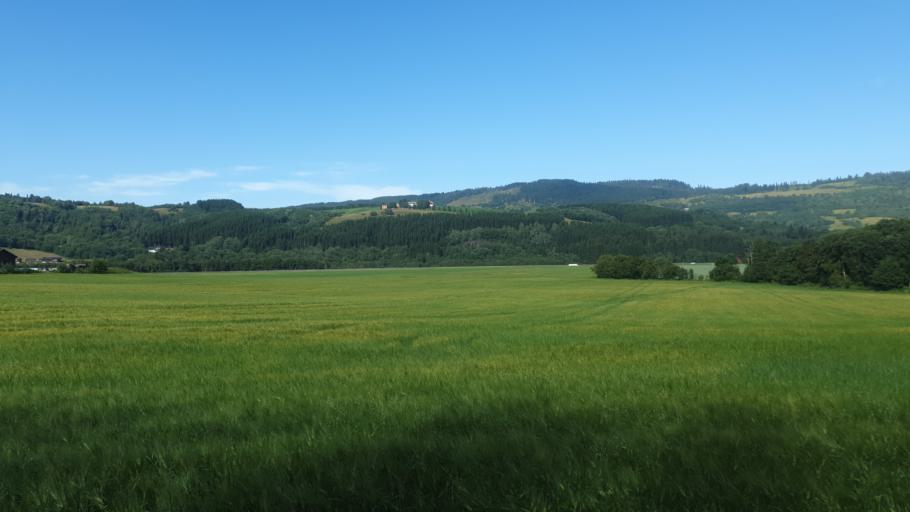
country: NO
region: Sor-Trondelag
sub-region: Orkdal
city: Orkanger
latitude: 63.2692
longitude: 9.8171
